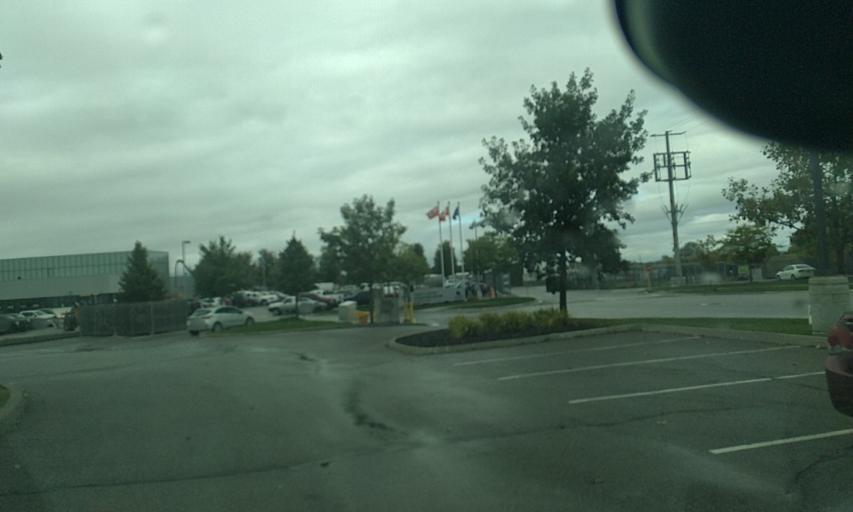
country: CA
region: Ontario
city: Newmarket
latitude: 44.0514
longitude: -79.4225
